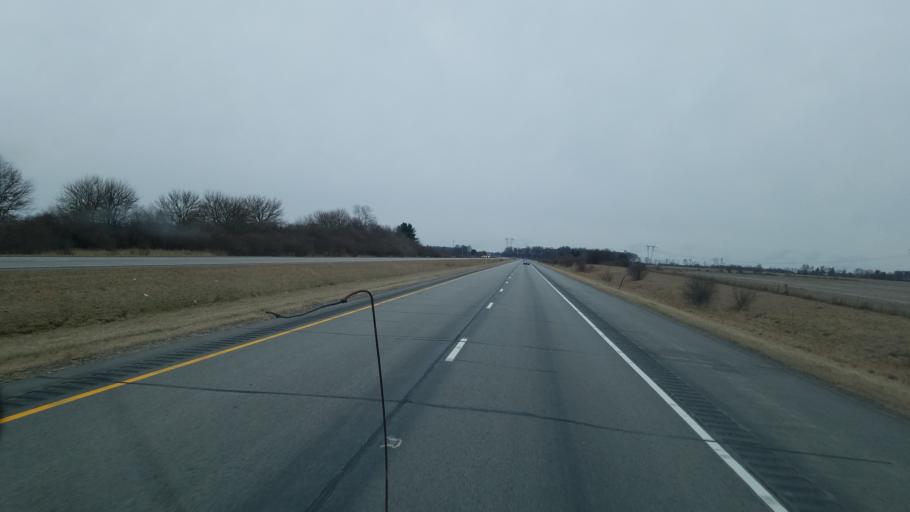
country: US
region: Indiana
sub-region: Marshall County
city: Argos
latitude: 41.2232
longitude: -86.2613
